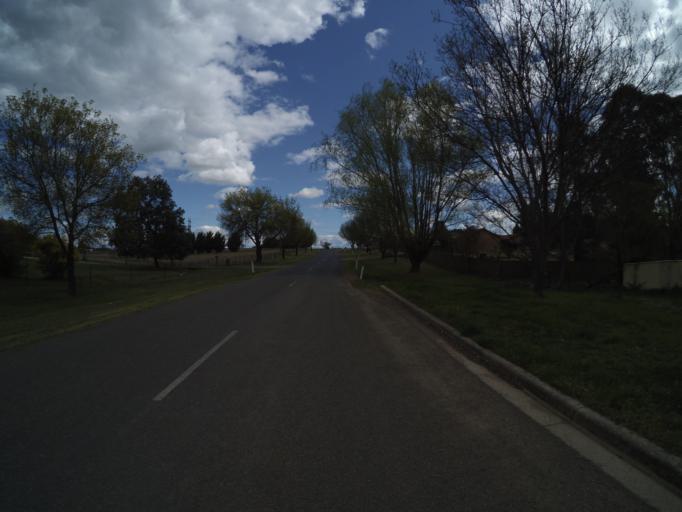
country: AU
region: New South Wales
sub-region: Yass Valley
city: Yass
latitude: -34.8584
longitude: 148.9181
